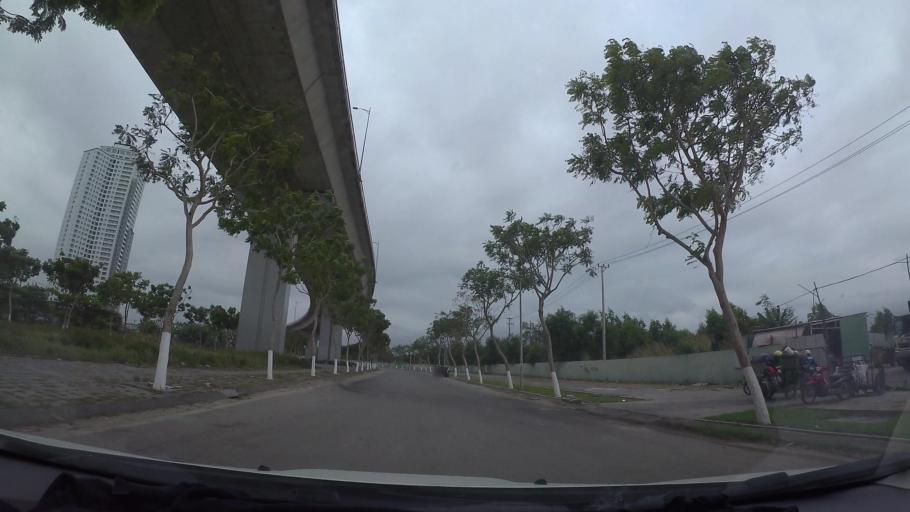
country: VN
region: Da Nang
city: Da Nang
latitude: 16.0934
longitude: 108.2168
